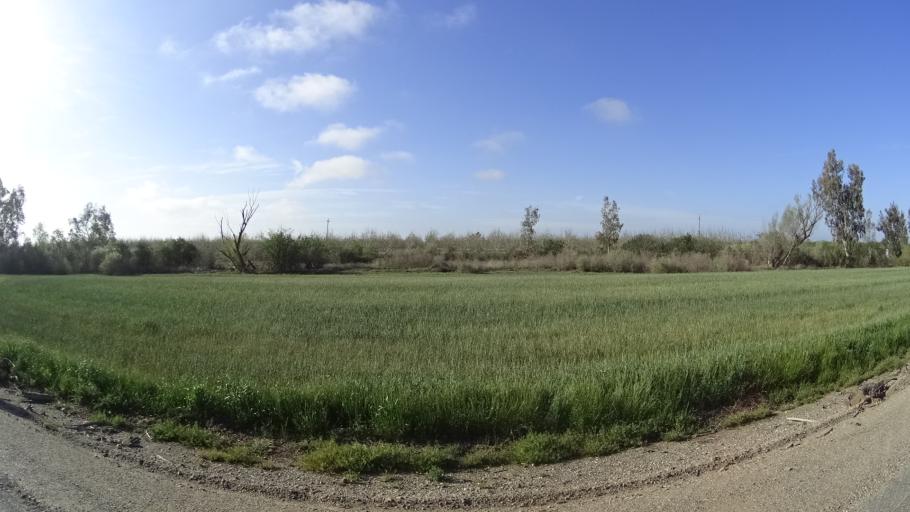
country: US
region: California
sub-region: Glenn County
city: Willows
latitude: 39.5824
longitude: -122.1825
